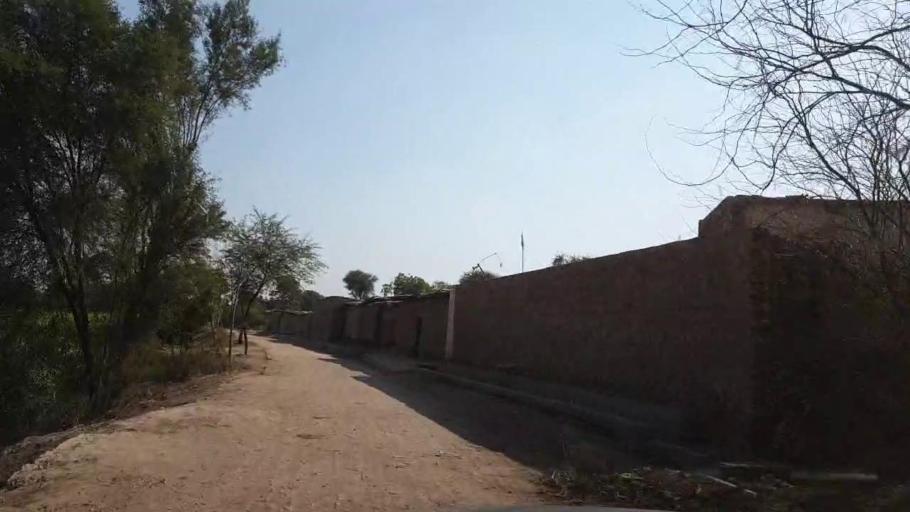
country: PK
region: Sindh
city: Tando Allahyar
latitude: 25.5839
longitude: 68.7534
